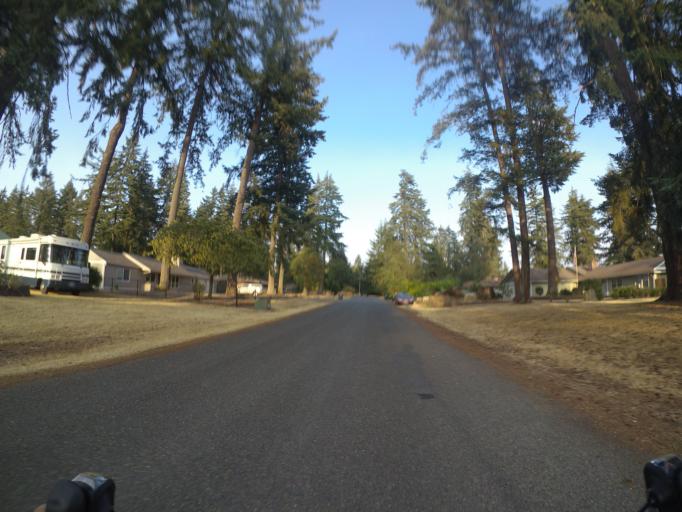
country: US
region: Washington
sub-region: Pierce County
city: Lakewood
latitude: 47.1468
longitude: -122.5153
